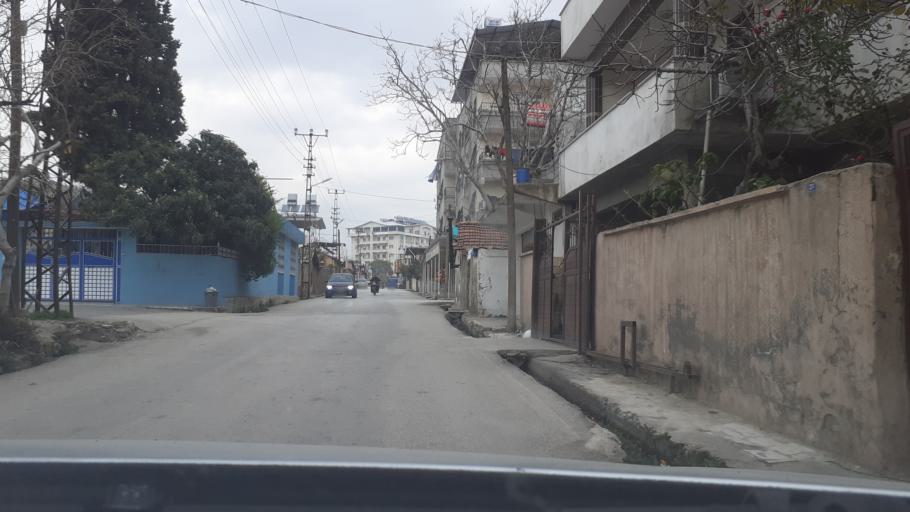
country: TR
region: Hatay
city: Kirikhan
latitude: 36.4955
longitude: 36.3514
